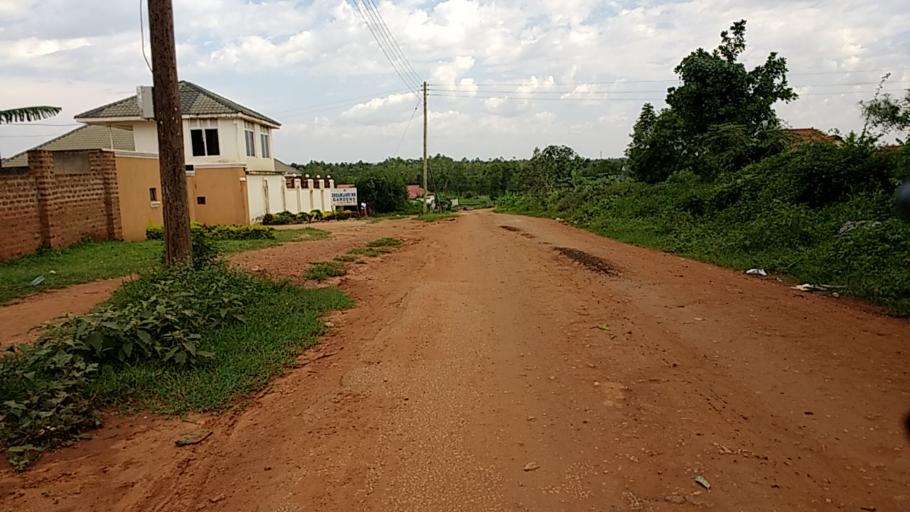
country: UG
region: Eastern Region
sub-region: Mbale District
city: Mbale
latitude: 1.0683
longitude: 34.1696
